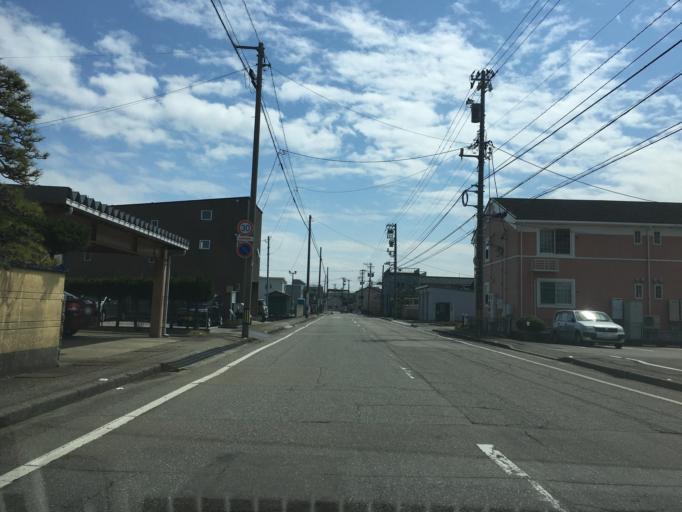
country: JP
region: Toyama
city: Nishishinminato
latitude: 36.7990
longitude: 137.0557
